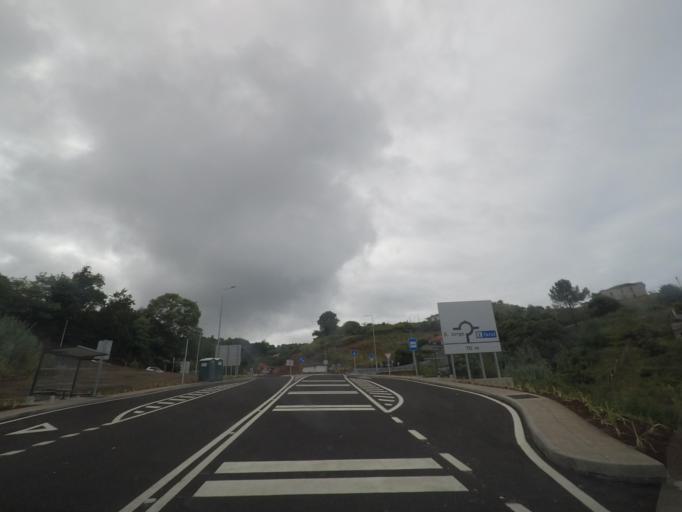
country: PT
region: Madeira
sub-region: Santana
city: Santana
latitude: 32.8302
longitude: -16.9070
